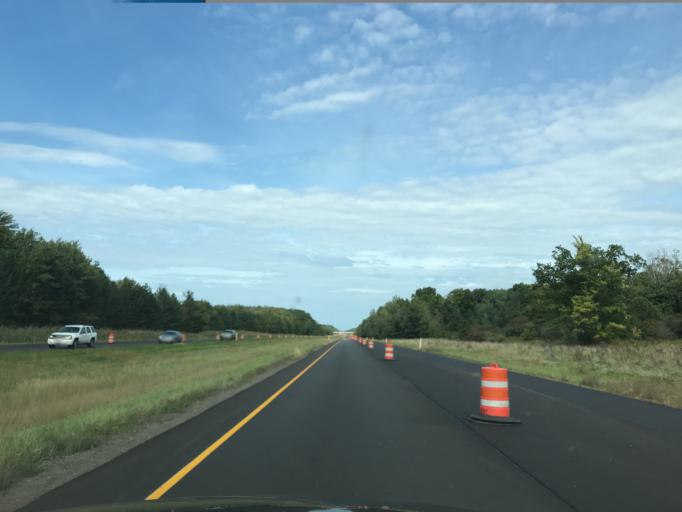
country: US
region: Ohio
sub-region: Ashtabula County
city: Jefferson
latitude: 41.7718
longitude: -80.7255
